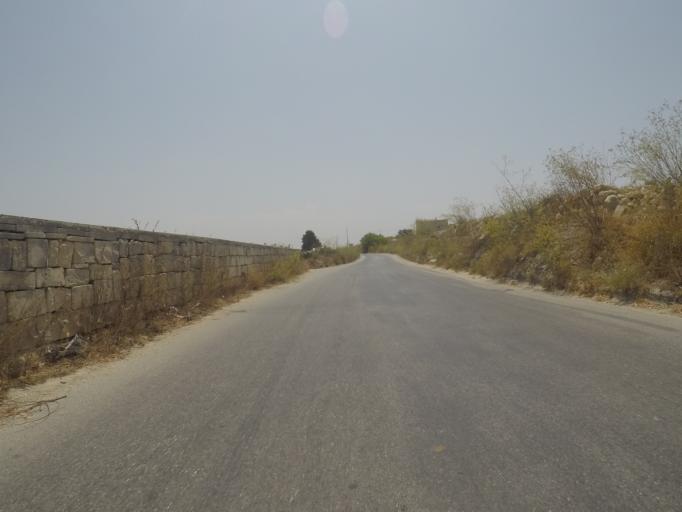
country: MT
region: Ir-Rabat
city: Rabat
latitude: 35.8681
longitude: 14.4159
